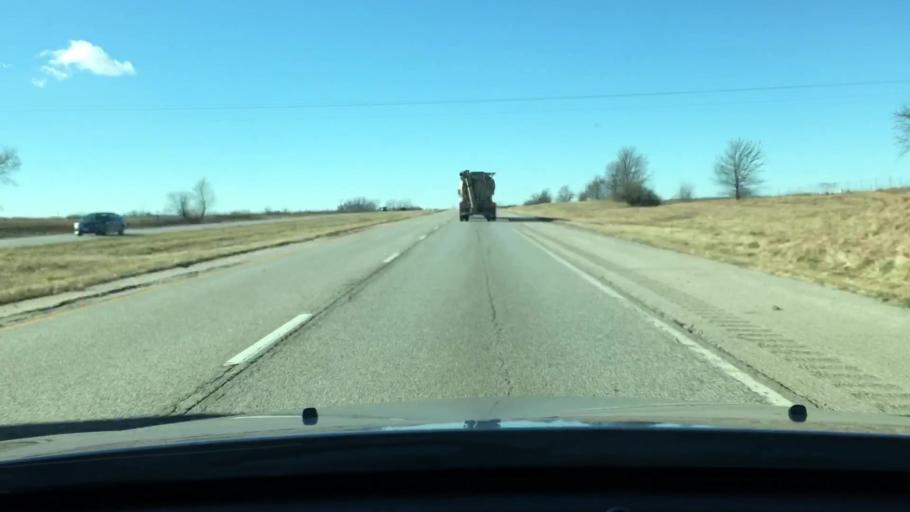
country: US
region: Illinois
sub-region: Pike County
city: Griggsville
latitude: 39.6783
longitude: -90.7039
